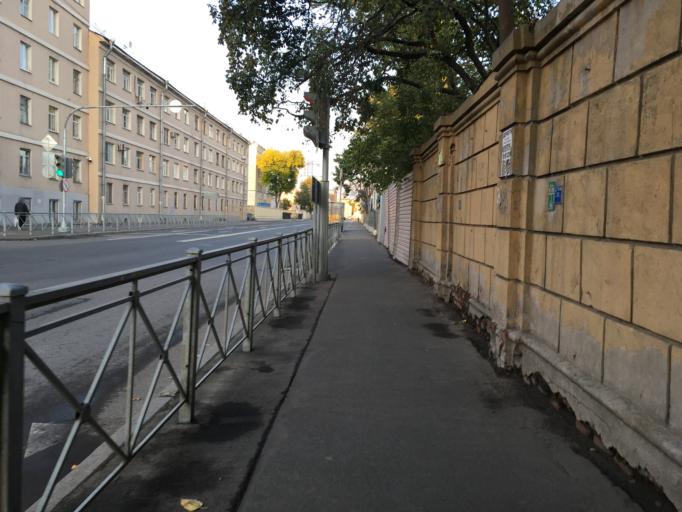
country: RU
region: St.-Petersburg
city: Saint Petersburg
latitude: 59.9033
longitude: 30.3281
